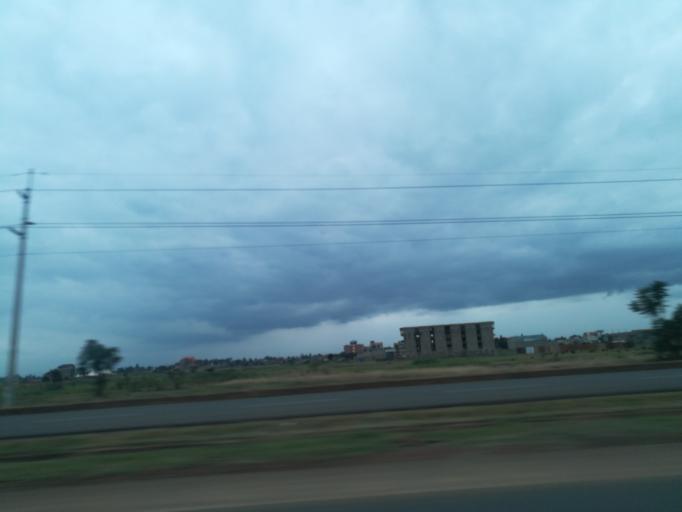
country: KE
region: Nairobi Area
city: Thika
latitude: -1.0471
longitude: 37.0593
